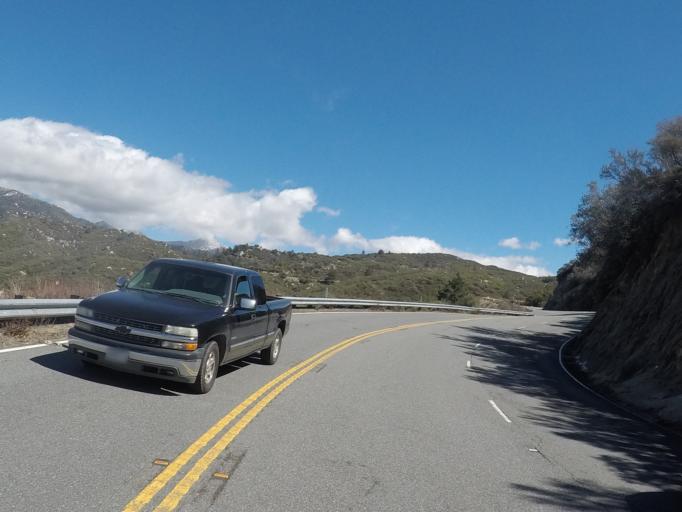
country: US
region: California
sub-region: Riverside County
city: Idyllwild
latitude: 33.7019
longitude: -116.7458
